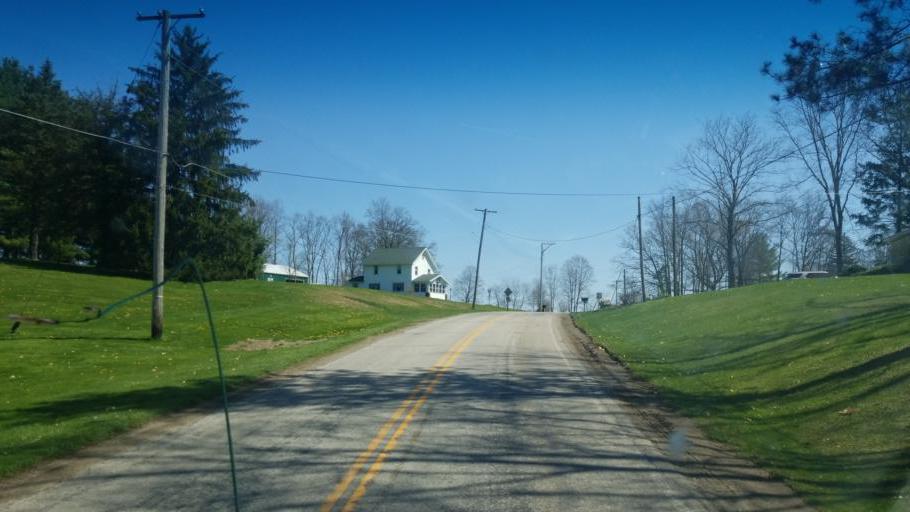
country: US
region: Ohio
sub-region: Richland County
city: Lincoln Heights
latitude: 40.8129
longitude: -82.4309
